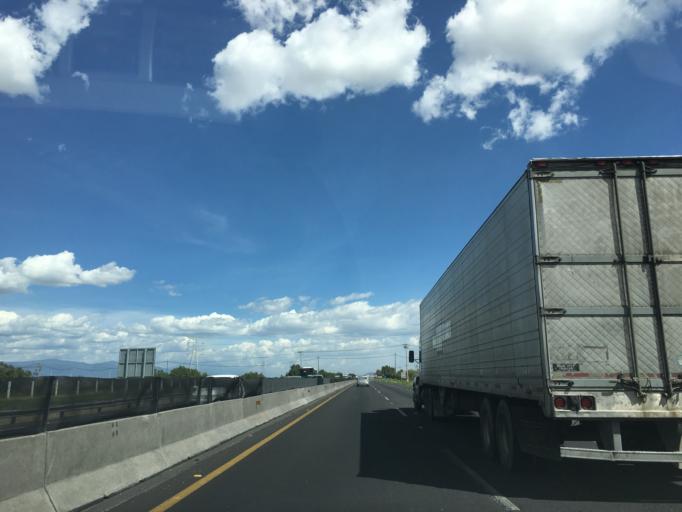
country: MX
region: Mexico
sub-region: Jaltenco
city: Alborada Jaltenco
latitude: 19.6726
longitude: -99.0698
